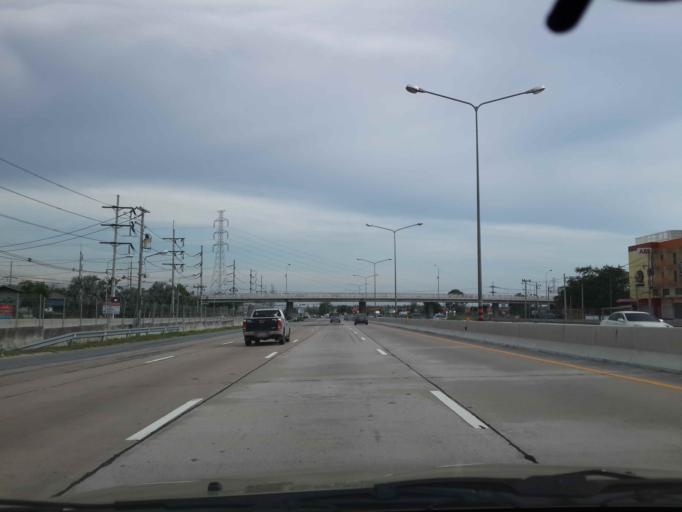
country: TH
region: Chon Buri
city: Si Racha
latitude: 13.1559
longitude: 100.9873
